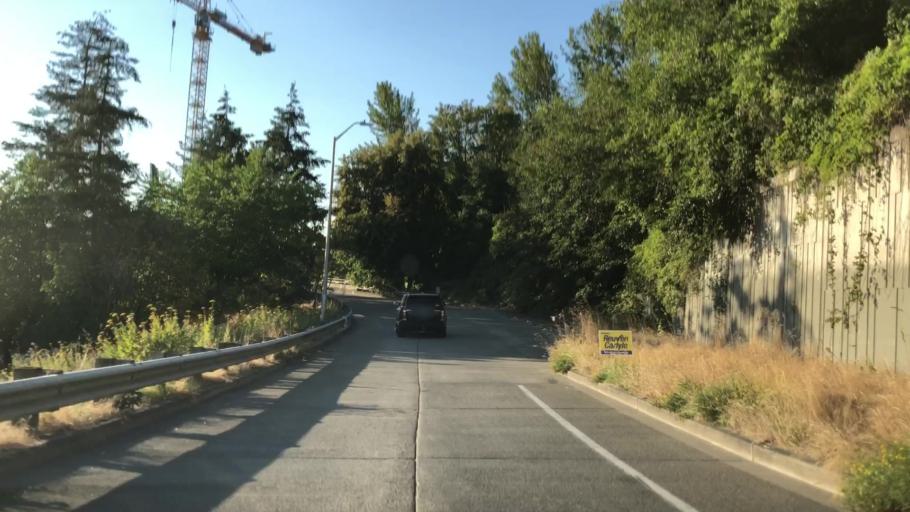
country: US
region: Washington
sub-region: King County
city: Seattle
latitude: 47.6328
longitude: -122.3745
